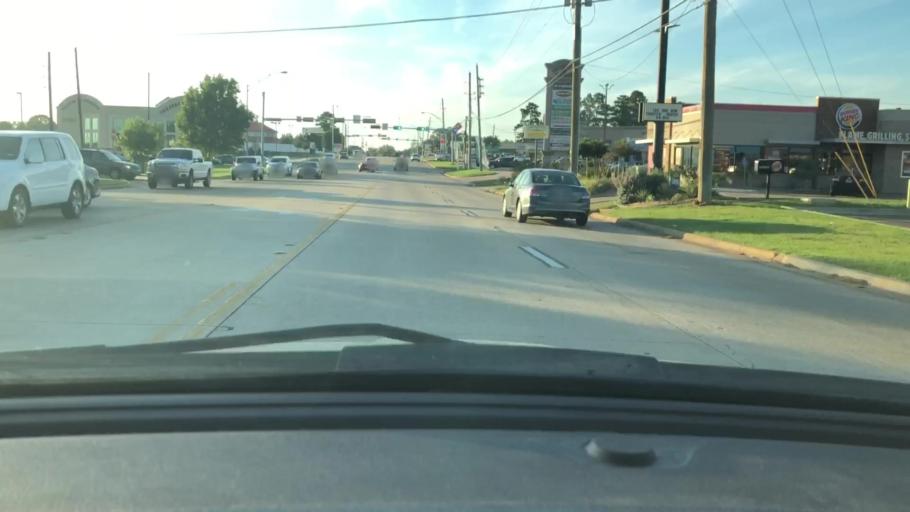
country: US
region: Texas
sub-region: Bowie County
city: Wake Village
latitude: 33.4586
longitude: -94.0889
